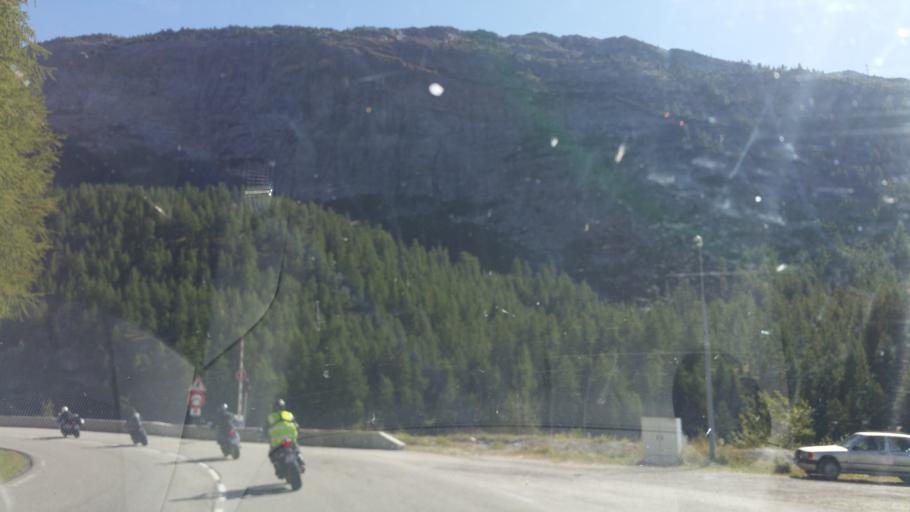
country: FR
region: Rhone-Alpes
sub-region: Departement de la Savoie
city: Tignes
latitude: 45.4745
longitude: 6.9485
